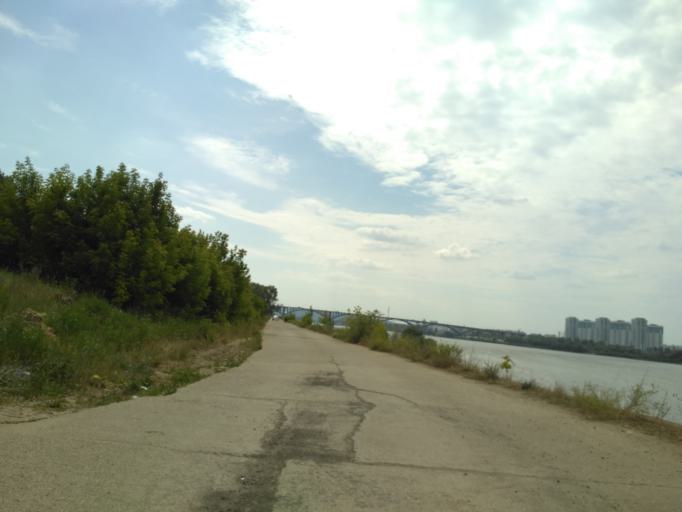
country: RU
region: Nizjnij Novgorod
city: Nizhniy Novgorod
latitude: 56.3139
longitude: 43.9687
